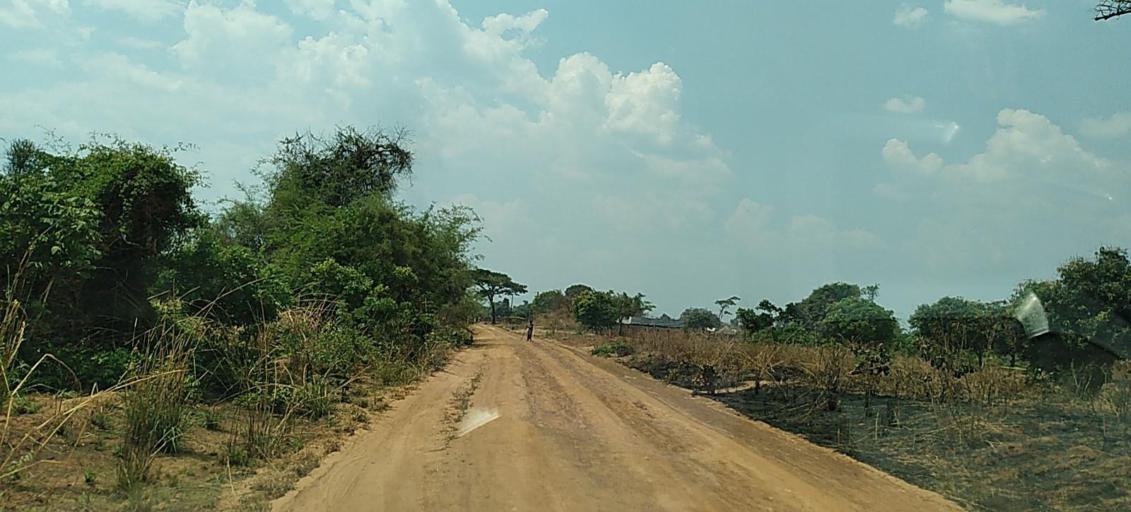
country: ZM
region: Copperbelt
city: Chingola
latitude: -12.5948
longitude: 27.7121
